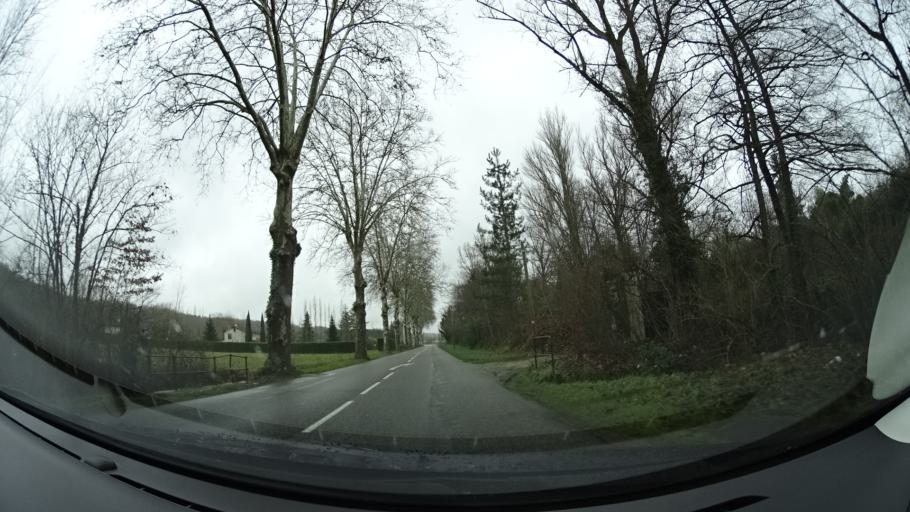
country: FR
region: Midi-Pyrenees
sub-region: Departement du Tarn-et-Garonne
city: Moissac
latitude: 44.1316
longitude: 1.1012
